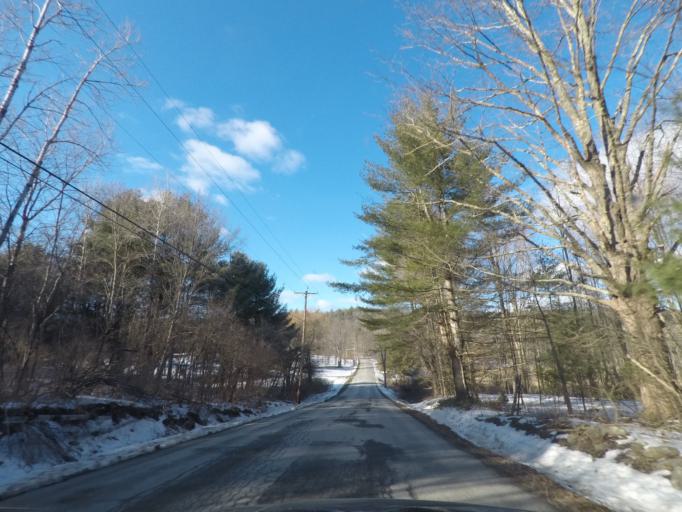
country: US
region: New York
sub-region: Rensselaer County
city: Averill Park
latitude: 42.5541
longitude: -73.5259
